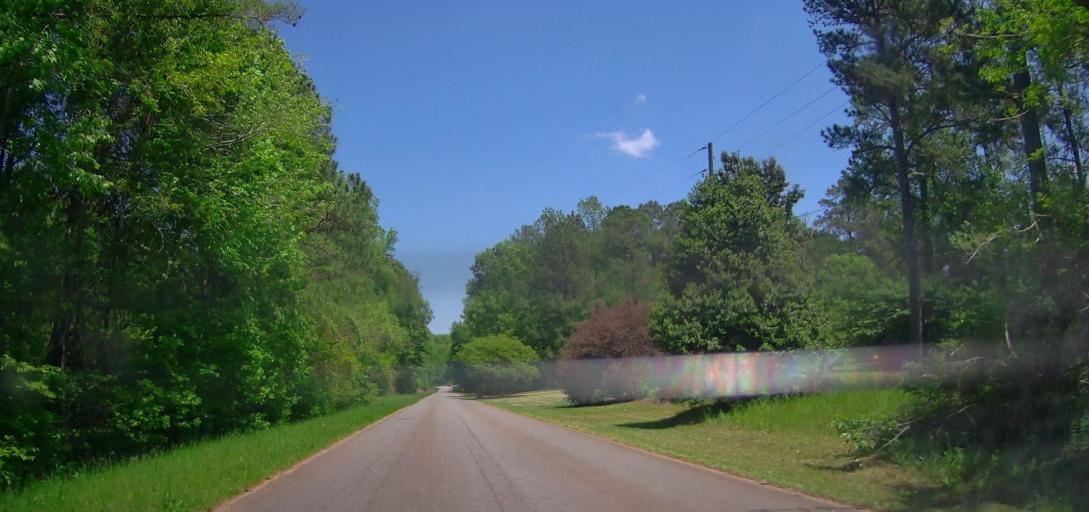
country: US
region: Georgia
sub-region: Jasper County
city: Monticello
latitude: 33.3252
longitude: -83.7087
